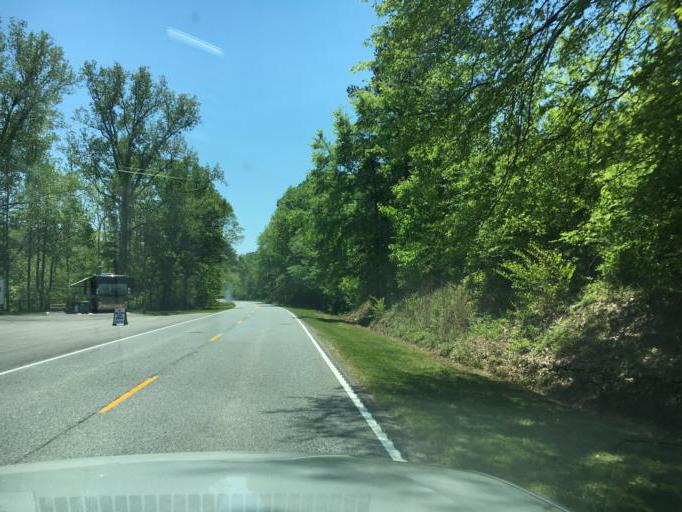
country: US
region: South Carolina
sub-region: Cherokee County
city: Blacksburg
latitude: 35.1358
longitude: -81.5816
